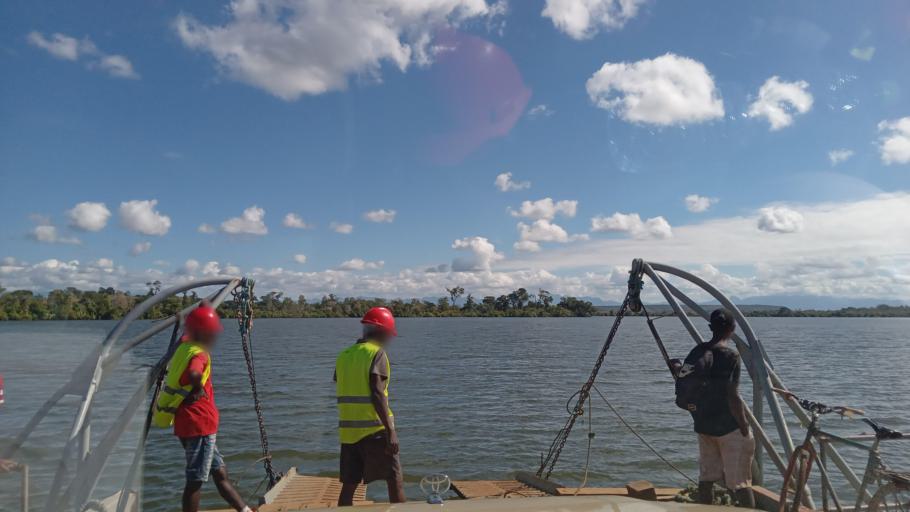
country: MG
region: Atsimo-Atsinanana
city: Vohipaho
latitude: -23.8142
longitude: 47.5487
